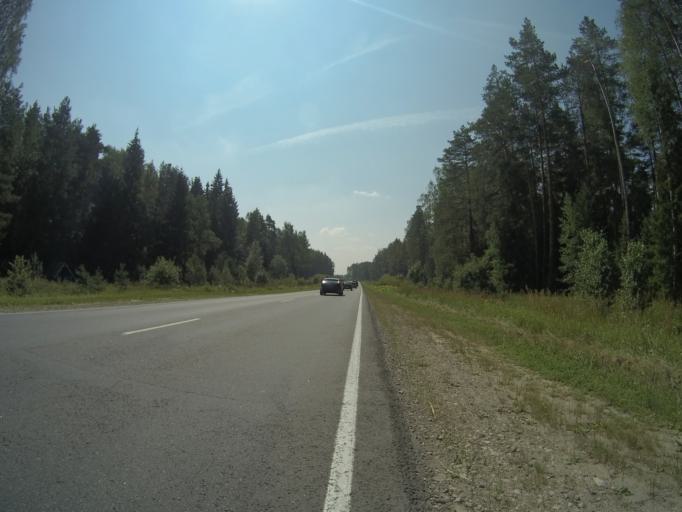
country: RU
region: Vladimir
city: Anopino
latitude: 55.7142
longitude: 40.7269
